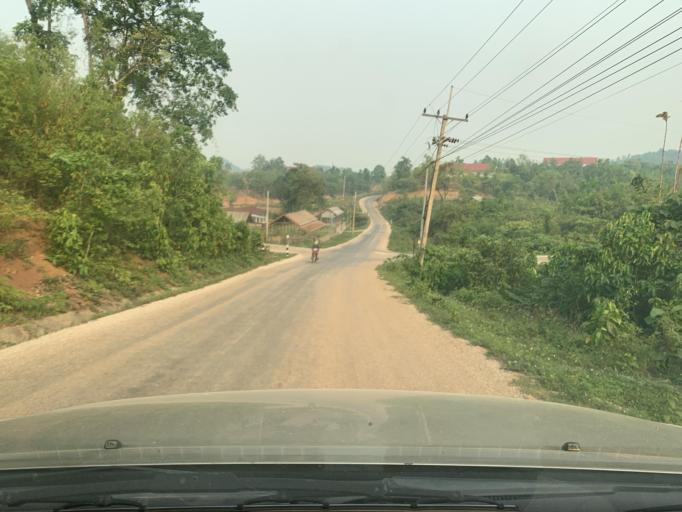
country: LA
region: Louangphabang
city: Louangphabang
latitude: 19.9104
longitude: 102.0813
